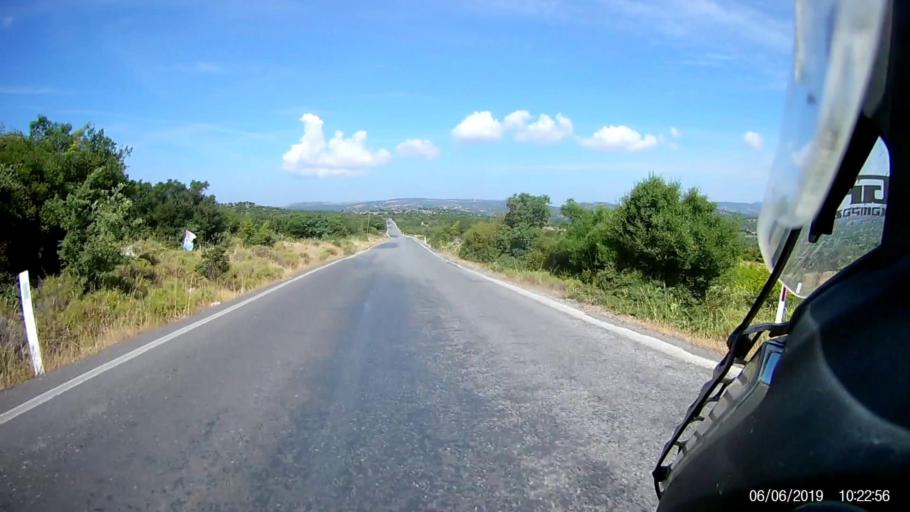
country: TR
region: Canakkale
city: Ayvacik
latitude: 39.5097
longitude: 26.4263
